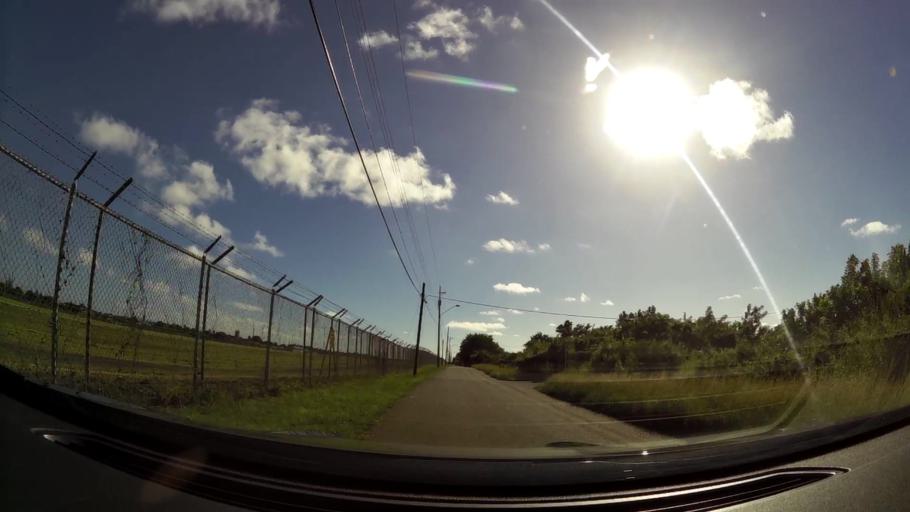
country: TT
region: Tobago
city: Scarborough
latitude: 11.1492
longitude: -60.8384
